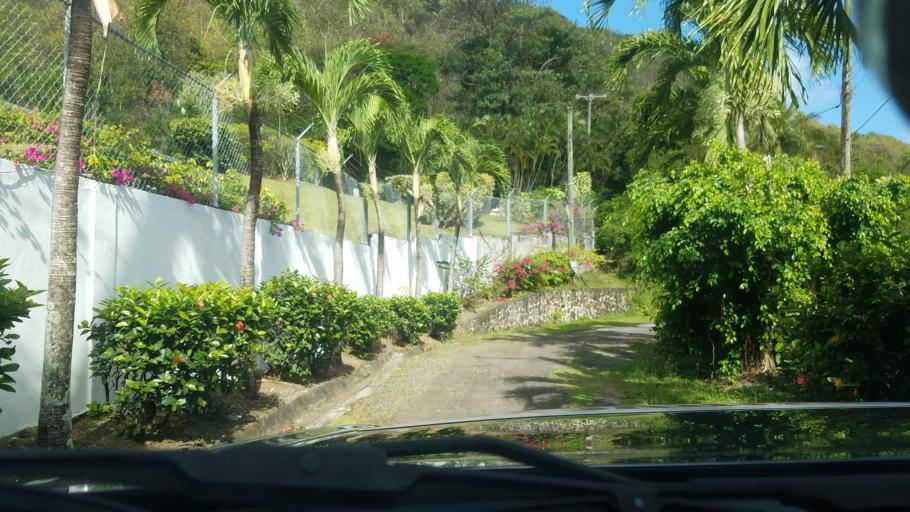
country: LC
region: Gros-Islet
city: Gros Islet
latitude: 14.0683
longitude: -60.9582
